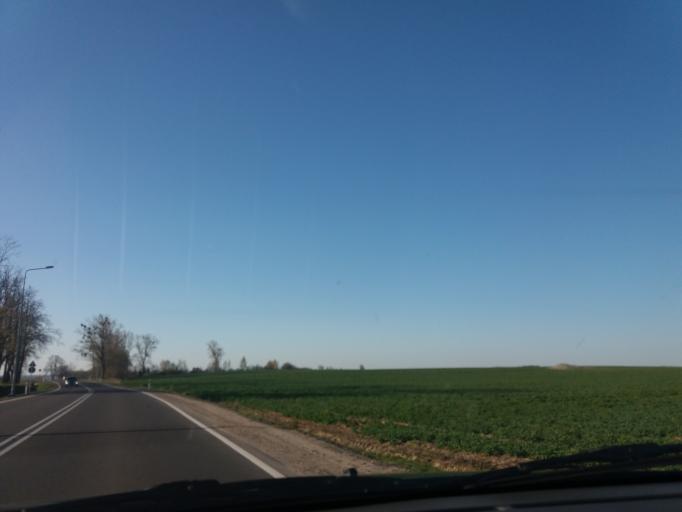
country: PL
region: Warmian-Masurian Voivodeship
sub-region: Powiat nidzicki
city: Nidzica
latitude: 53.3349
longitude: 20.4385
